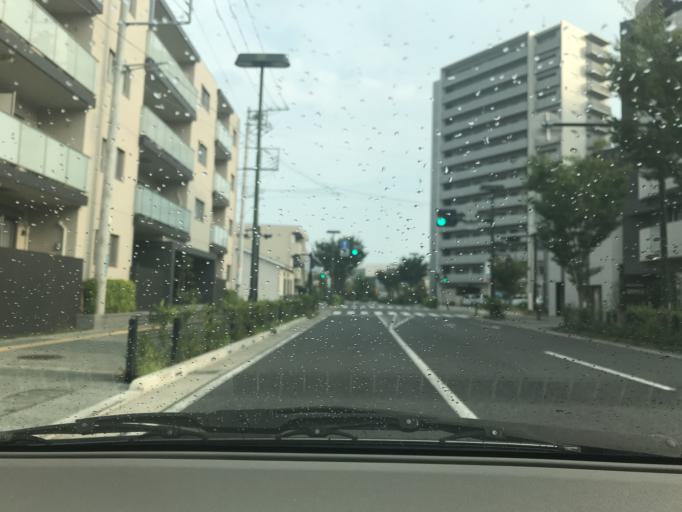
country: JP
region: Kanagawa
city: Fujisawa
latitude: 35.3439
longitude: 139.4462
